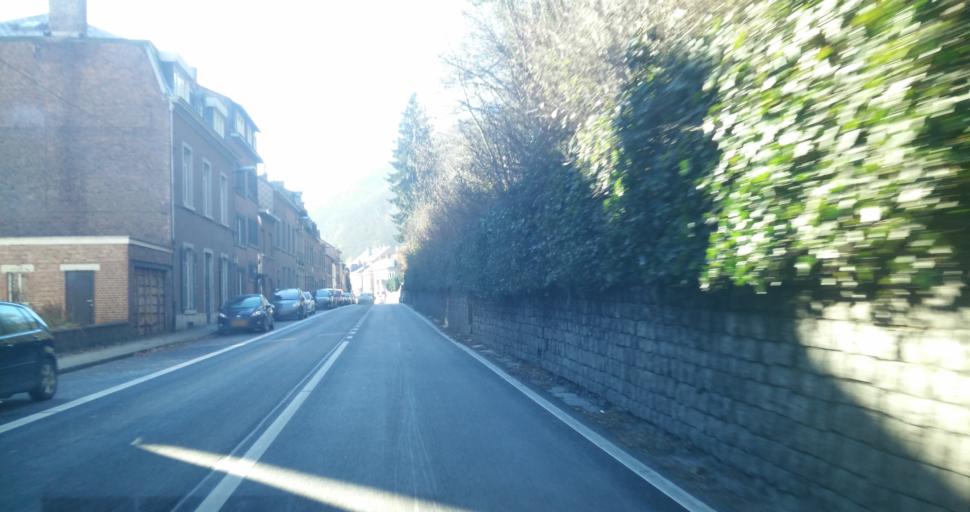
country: BE
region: Wallonia
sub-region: Province de Namur
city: Namur
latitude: 50.4521
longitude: 4.8581
